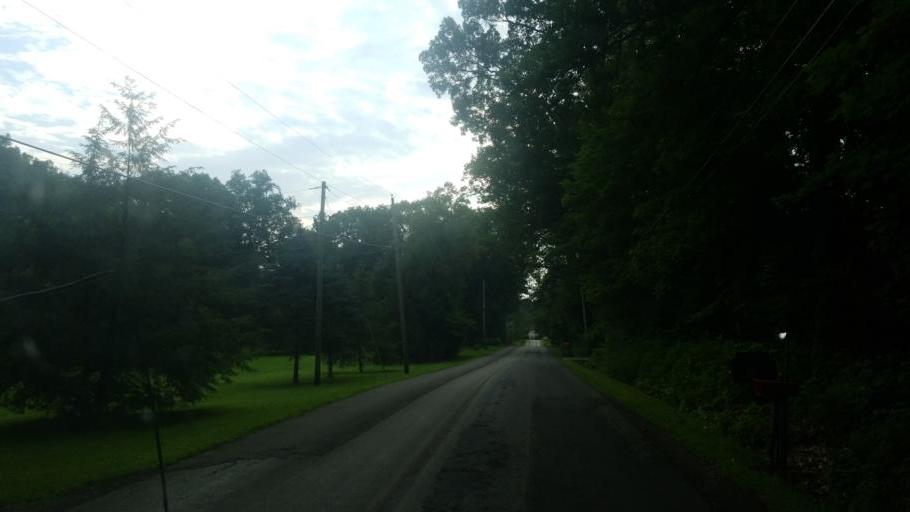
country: US
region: Ohio
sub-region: Wayne County
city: Wooster
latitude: 40.7847
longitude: -81.9876
